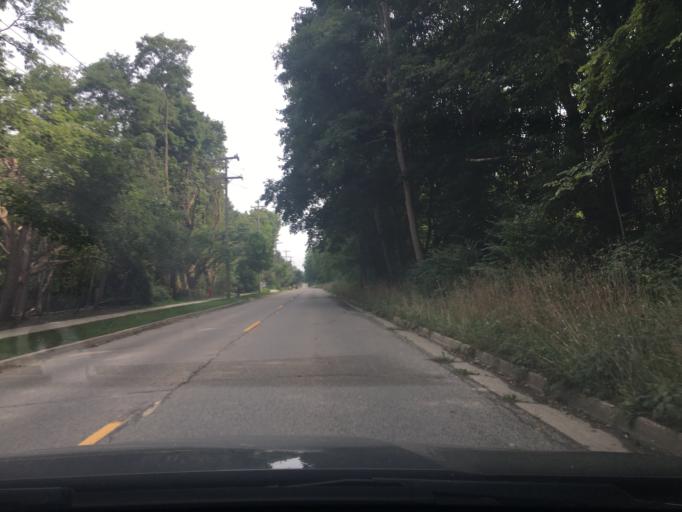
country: US
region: Michigan
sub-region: Oakland County
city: Birmingham
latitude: 42.5694
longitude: -83.2185
